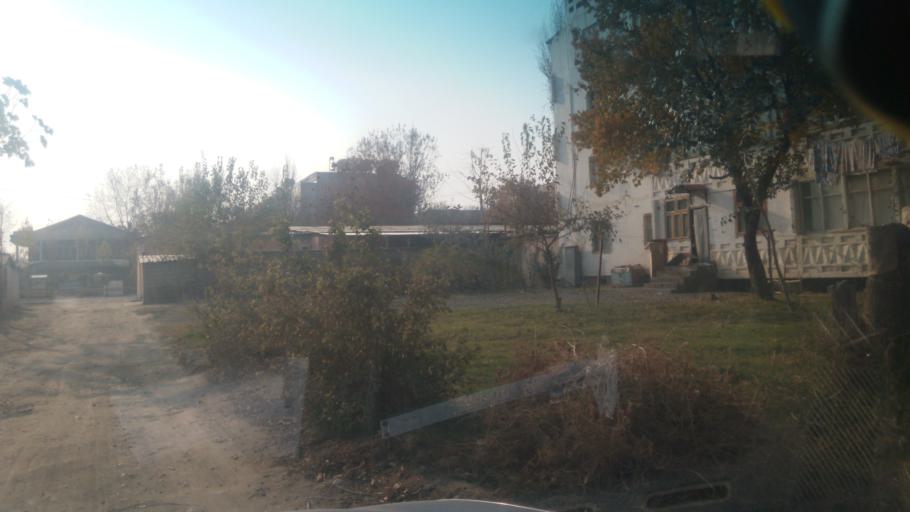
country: UZ
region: Sirdaryo
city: Guliston
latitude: 40.5193
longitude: 68.7757
